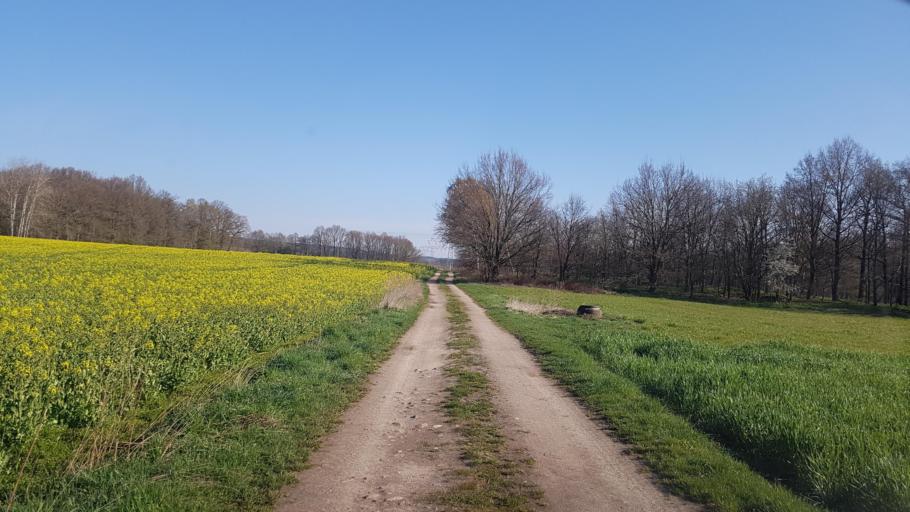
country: DE
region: Brandenburg
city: Altdobern
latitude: 51.6695
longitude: 13.9978
